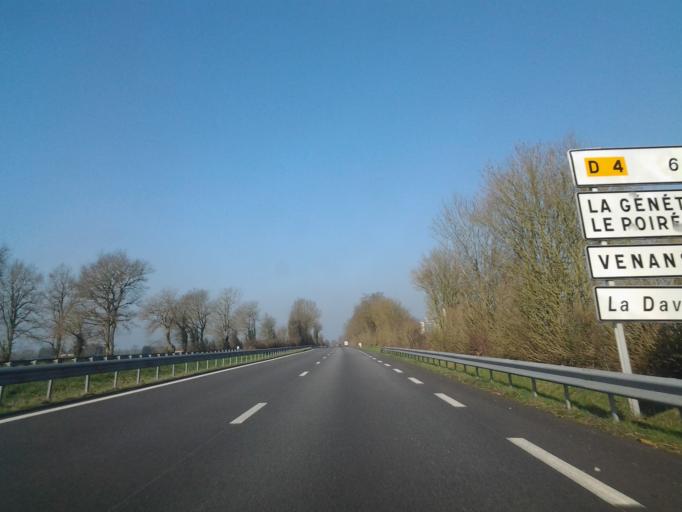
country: FR
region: Pays de la Loire
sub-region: Departement de la Vendee
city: Venansault
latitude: 46.7047
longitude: -1.5070
